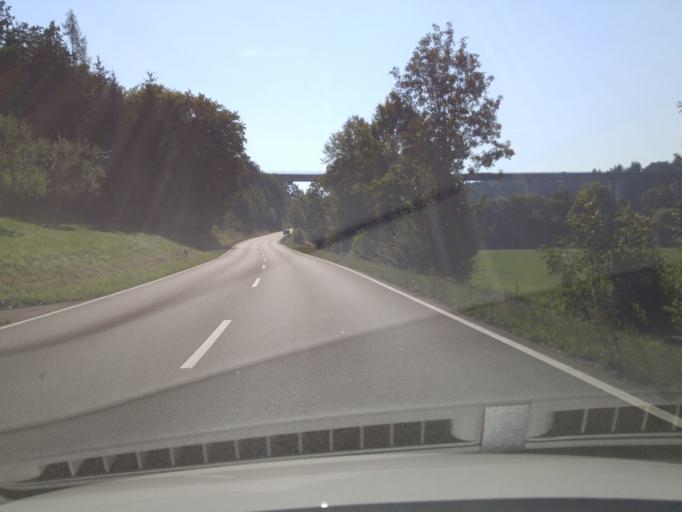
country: DE
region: Baden-Wuerttemberg
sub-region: Regierungsbezirk Stuttgart
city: Schlaitdorf
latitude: 48.6229
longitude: 9.2192
